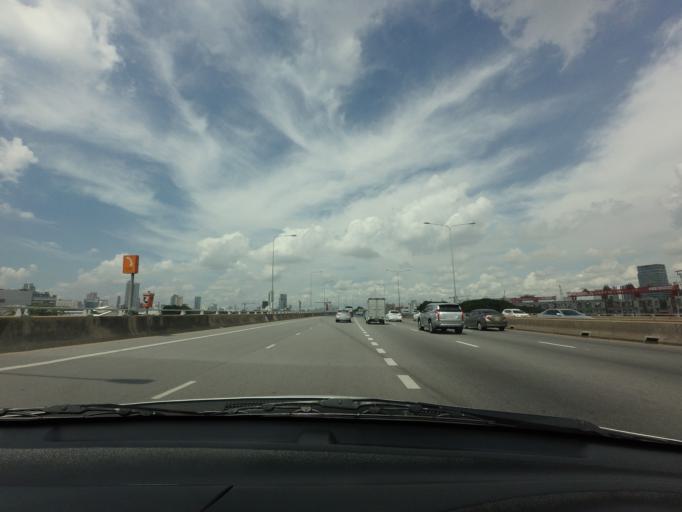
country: TH
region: Bangkok
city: Bang Sue
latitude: 13.8060
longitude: 100.5469
